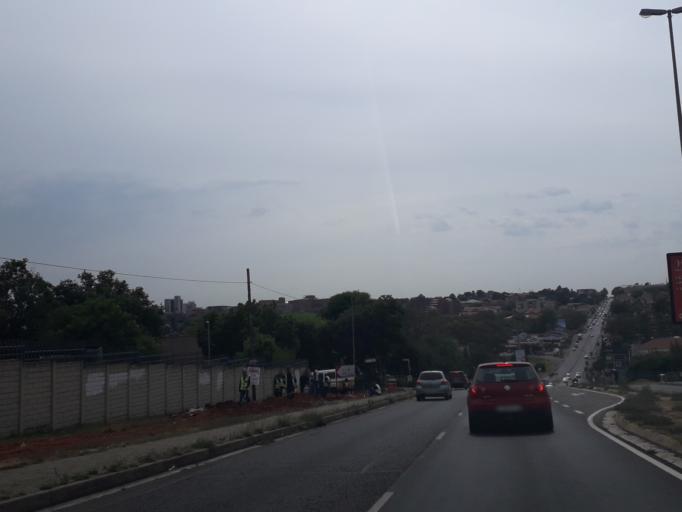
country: ZA
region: Gauteng
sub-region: City of Johannesburg Metropolitan Municipality
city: Johannesburg
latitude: -26.0982
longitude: 27.9879
